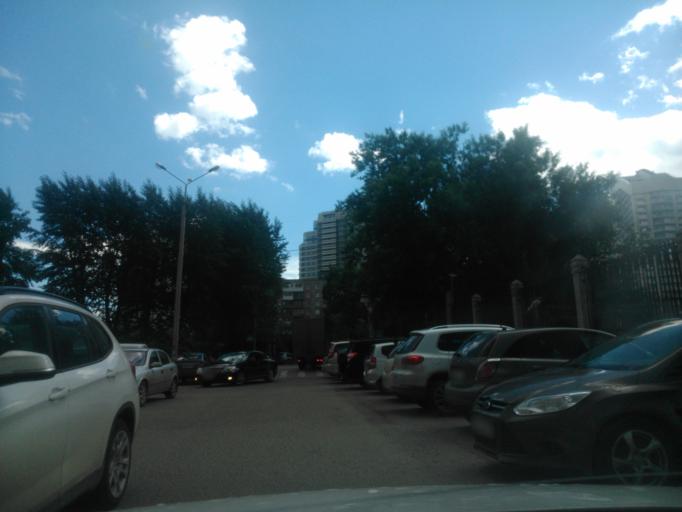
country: RU
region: Perm
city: Perm
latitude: 57.9992
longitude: 56.2679
